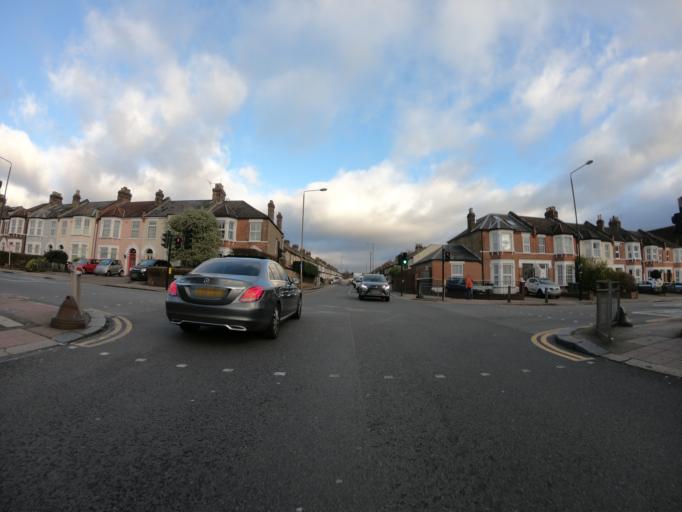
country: GB
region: England
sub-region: Greater London
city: Woolwich
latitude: 51.4611
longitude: 0.0575
